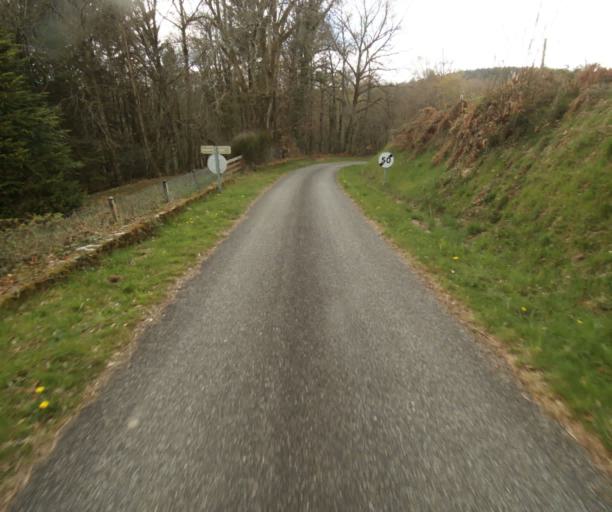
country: FR
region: Limousin
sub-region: Departement de la Correze
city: Laguenne
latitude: 45.2484
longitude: 1.8909
